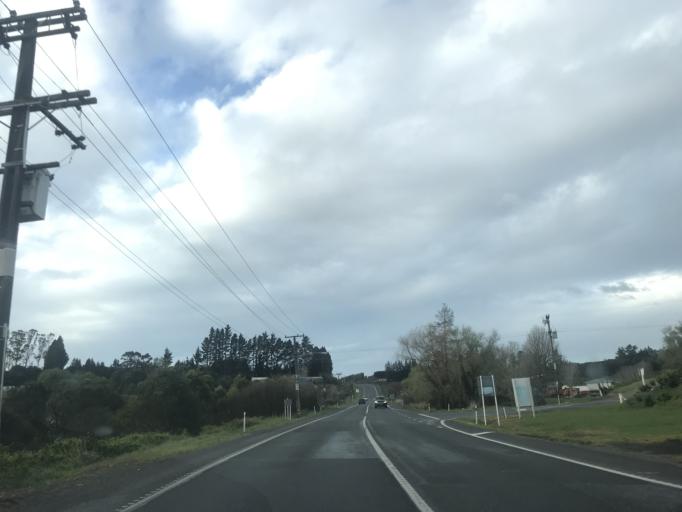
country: NZ
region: Bay of Plenty
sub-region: Western Bay of Plenty District
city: Katikati
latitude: -37.5452
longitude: 175.9107
